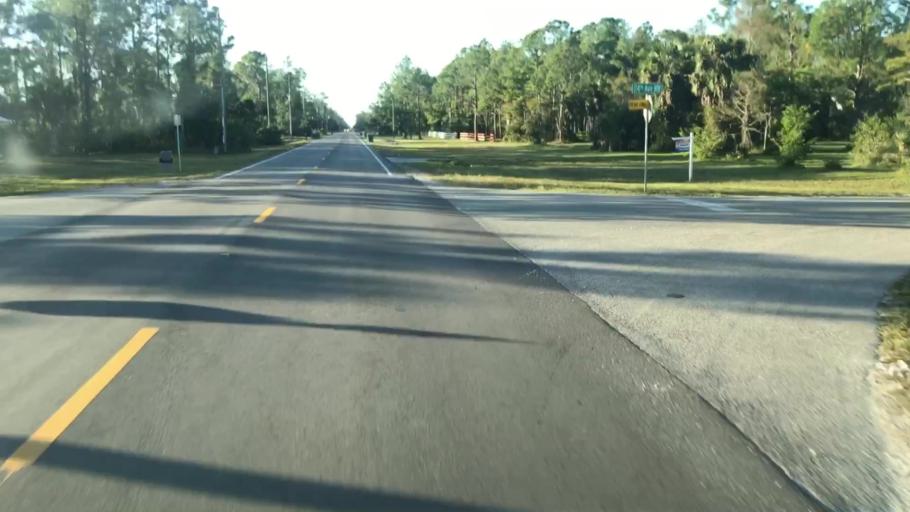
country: US
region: Florida
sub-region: Collier County
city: Orangetree
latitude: 26.2737
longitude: -81.6073
